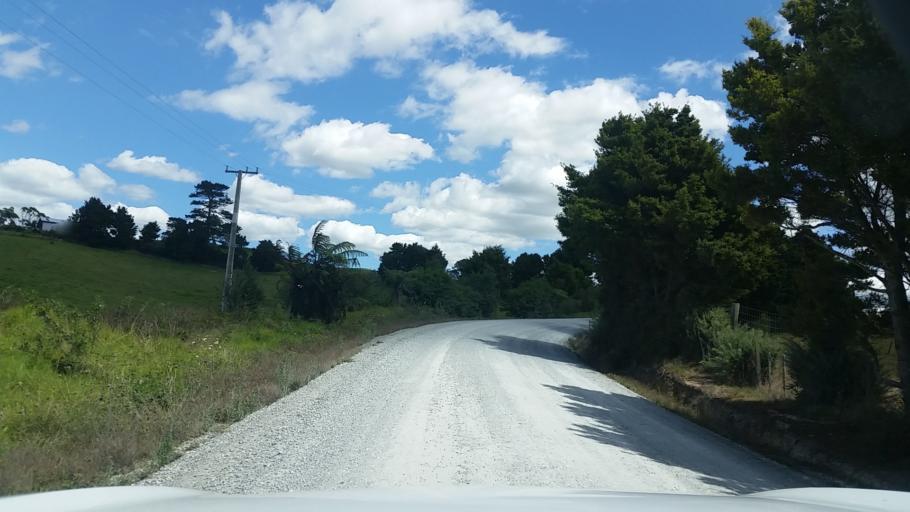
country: NZ
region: Northland
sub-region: Whangarei
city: Maungatapere
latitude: -35.6668
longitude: 174.1761
